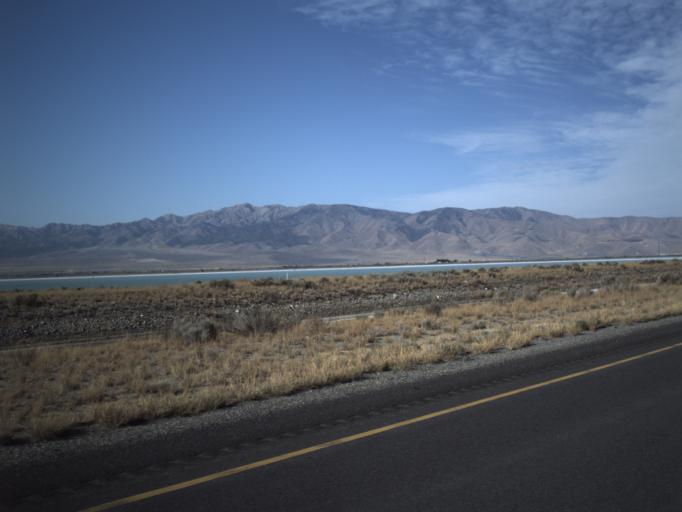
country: US
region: Utah
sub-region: Tooele County
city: Stansbury park
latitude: 40.6723
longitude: -112.3894
